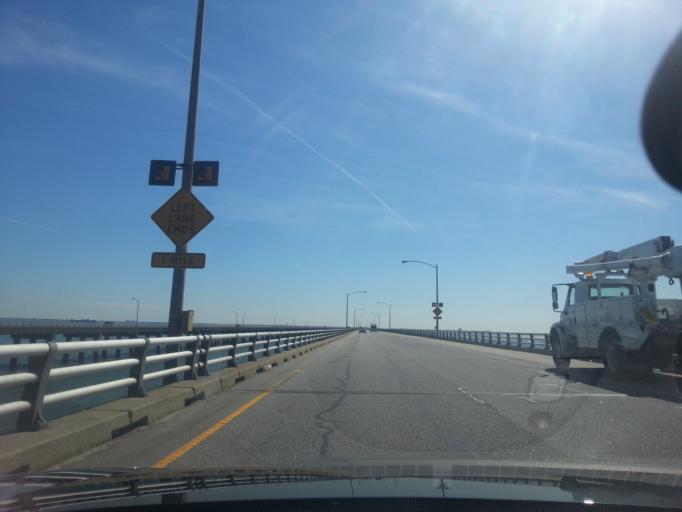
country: US
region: Virginia
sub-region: City of Virginia Beach
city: Virginia Beach
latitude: 37.0076
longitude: -76.0964
